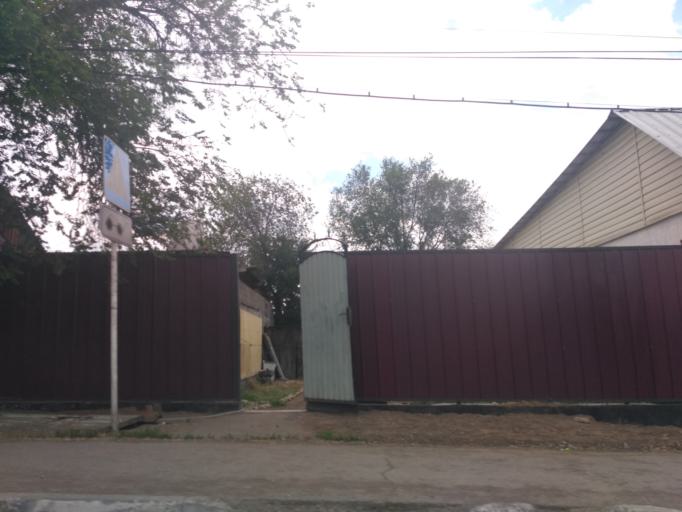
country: KZ
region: Almaty Oblysy
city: Burunday
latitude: 43.2020
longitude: 76.6347
